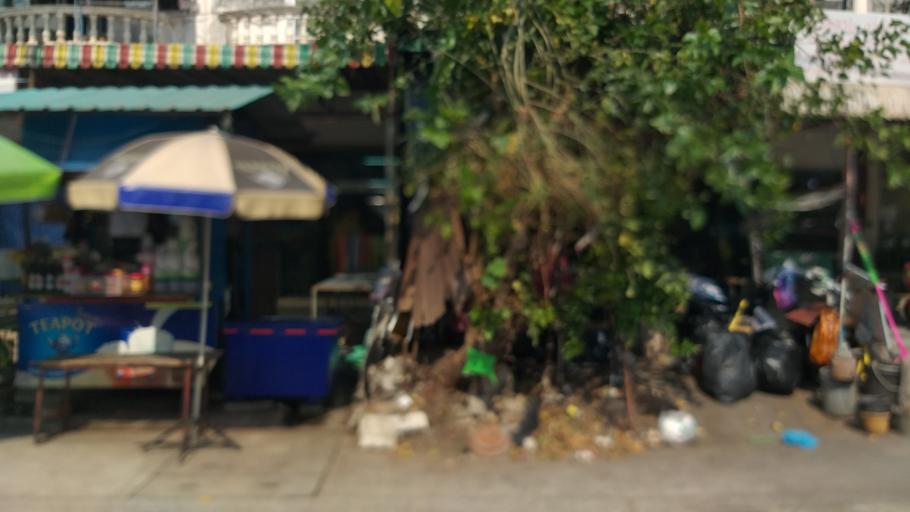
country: TH
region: Changwat Udon Thani
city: Udon Thani
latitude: 17.4140
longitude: 102.7764
